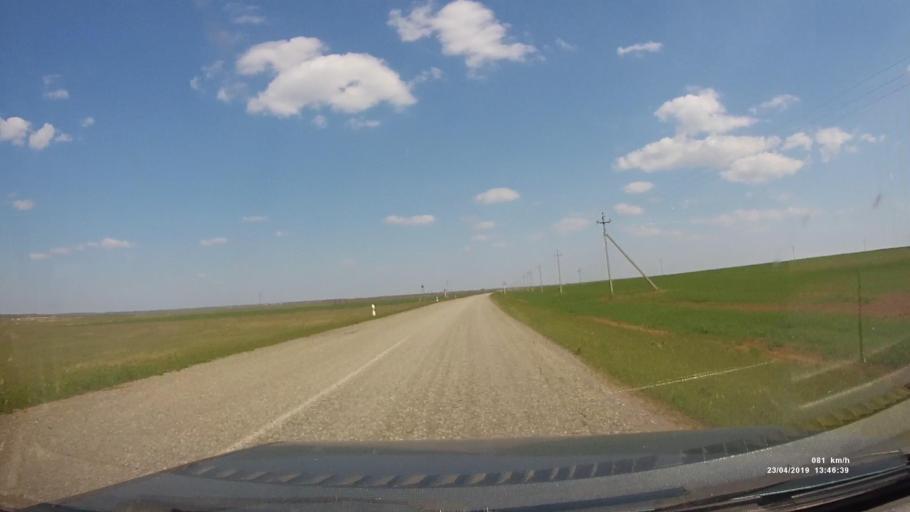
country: RU
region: Kalmykiya
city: Yashalta
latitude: 46.6000
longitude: 42.8379
